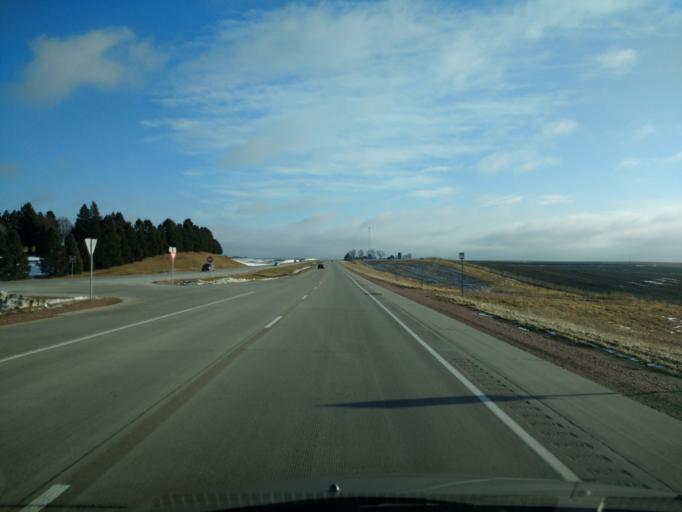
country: US
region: Iowa
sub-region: Ida County
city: Holstein
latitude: 42.4744
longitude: -95.5649
